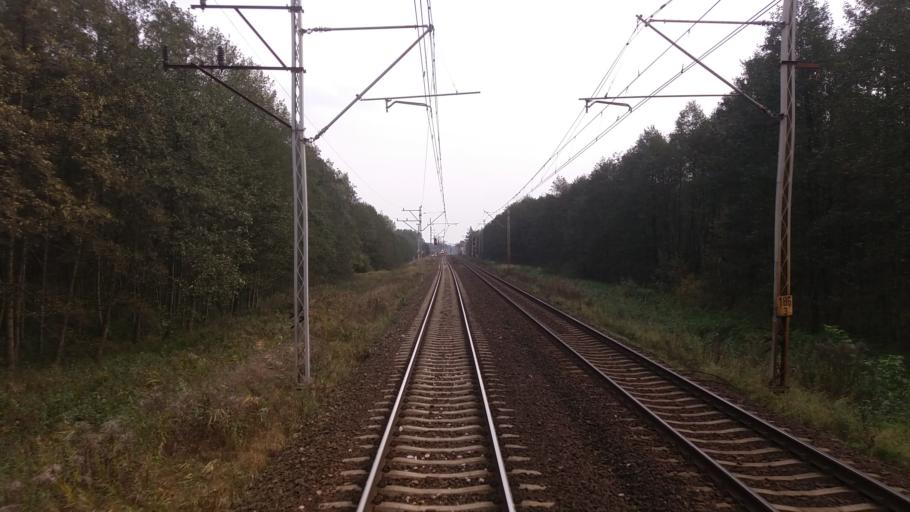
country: PL
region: West Pomeranian Voivodeship
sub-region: Powiat stargardzki
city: Kobylanka
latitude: 53.3737
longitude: 14.8516
